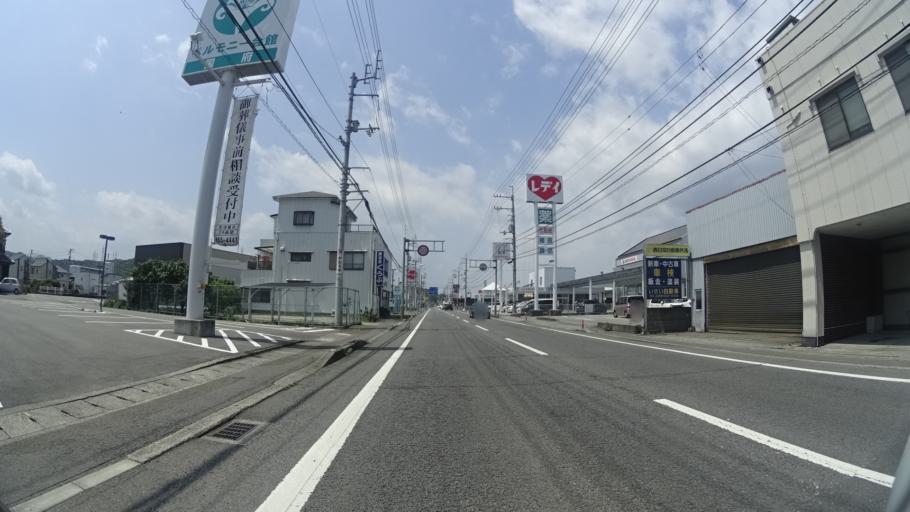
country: JP
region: Tokushima
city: Ishii
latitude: 34.0712
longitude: 134.4760
